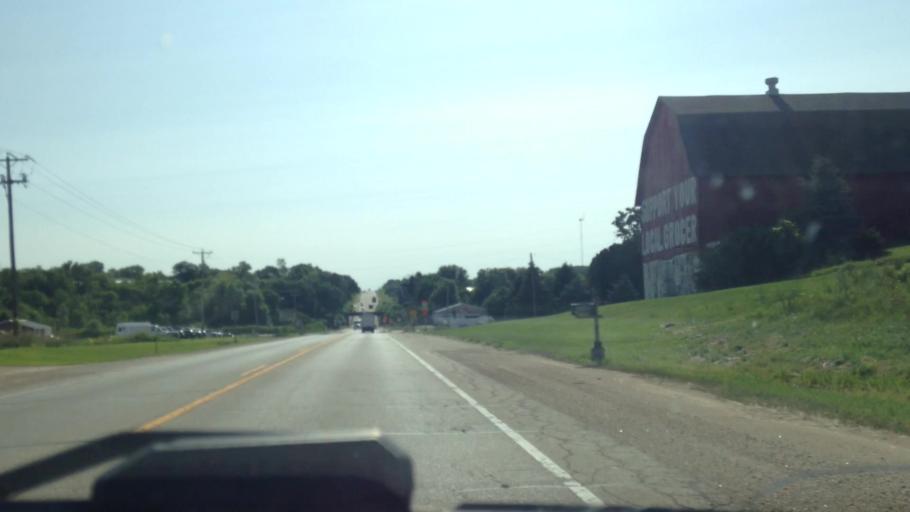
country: US
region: Wisconsin
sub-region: Dodge County
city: Mayville
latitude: 43.4428
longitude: -88.5471
